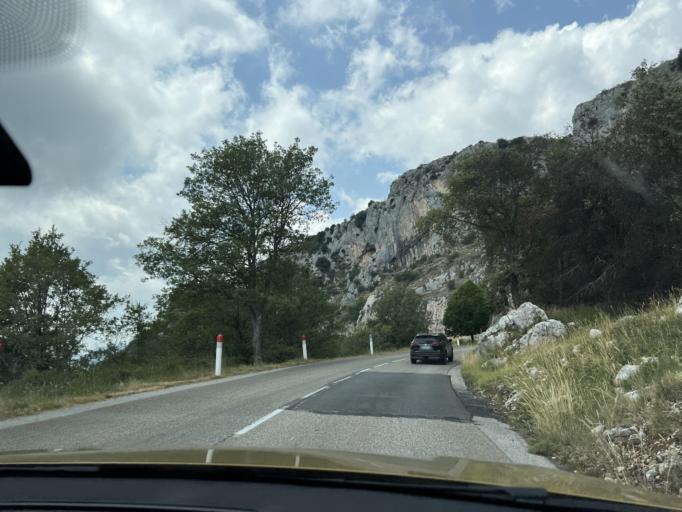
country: FR
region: Provence-Alpes-Cote d'Azur
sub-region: Departement des Alpes-Maritimes
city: Grasse
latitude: 43.7967
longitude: 6.9277
